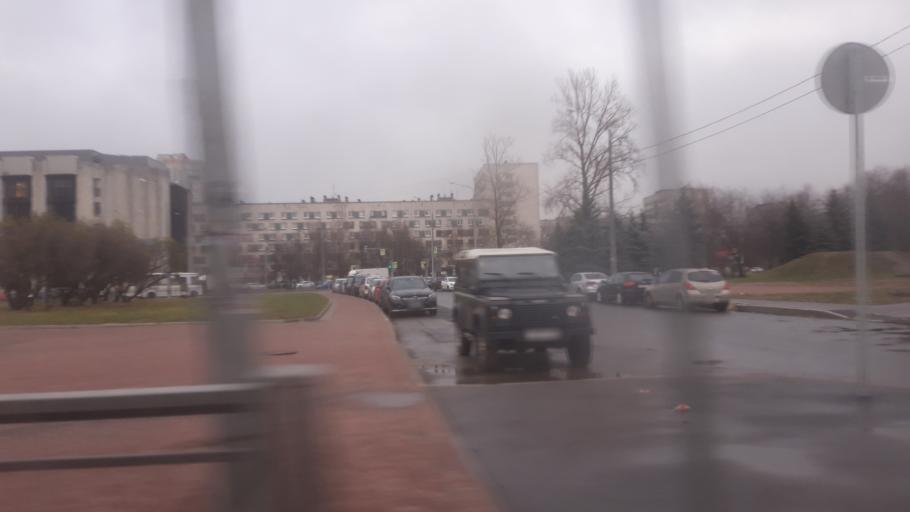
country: RU
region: St.-Petersburg
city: Kupchino
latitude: 59.8416
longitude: 30.3223
